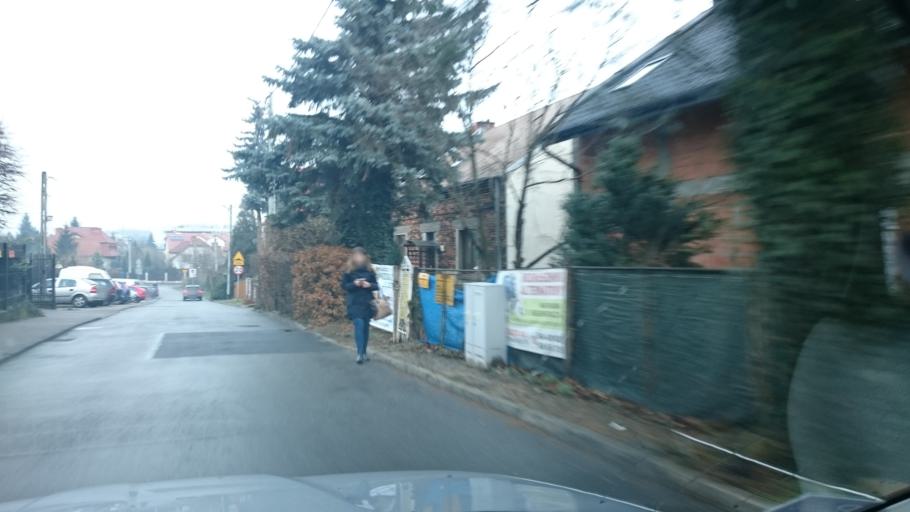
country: PL
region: Lesser Poland Voivodeship
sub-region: Krakow
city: Krakow
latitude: 50.0237
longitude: 19.9652
